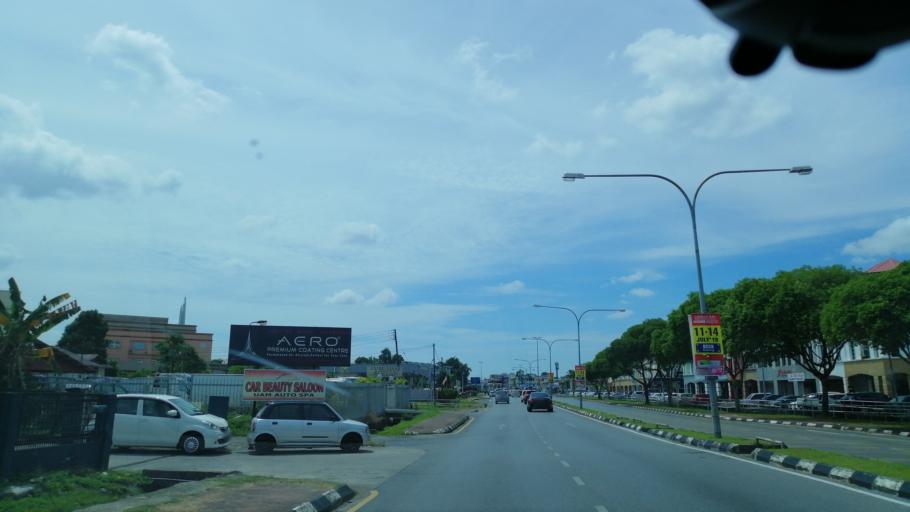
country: MY
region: Sarawak
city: Kuching
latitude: 1.5442
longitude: 110.3593
